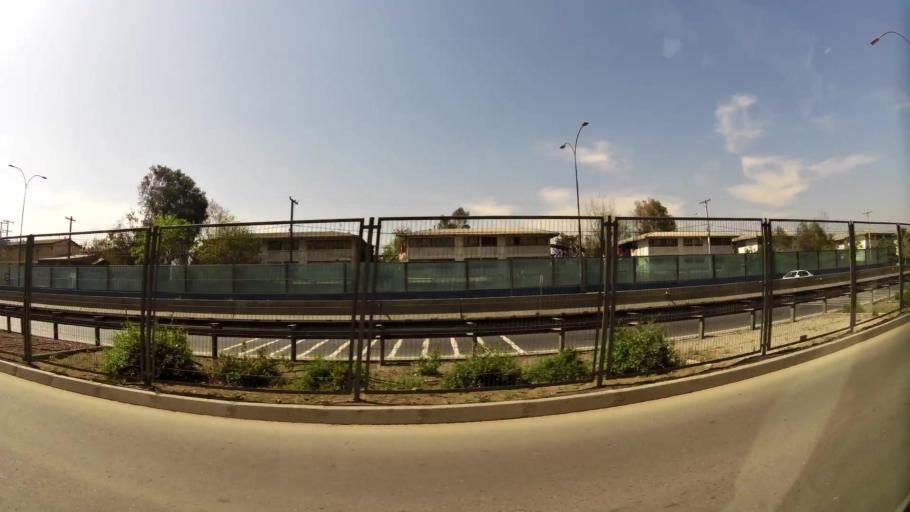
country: CL
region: Santiago Metropolitan
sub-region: Provincia de Santiago
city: Lo Prado
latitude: -33.3918
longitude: -70.7005
